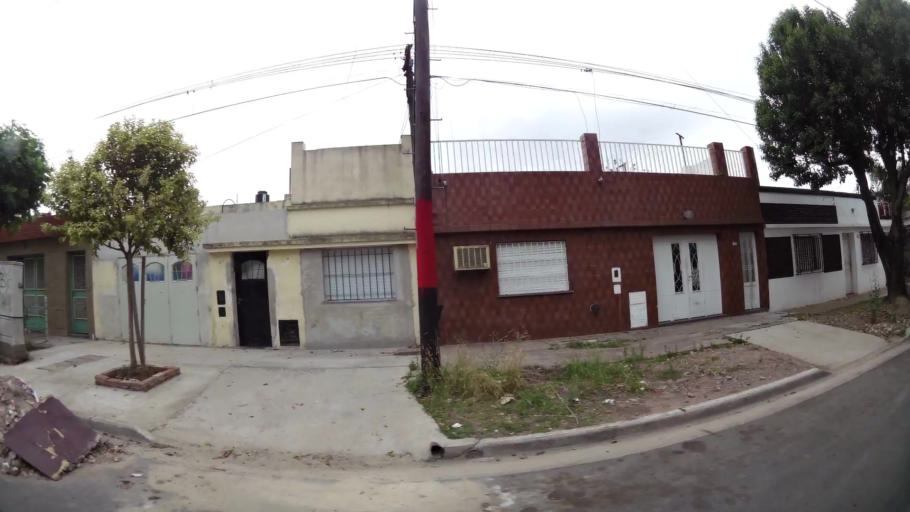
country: AR
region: Santa Fe
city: Gobernador Galvez
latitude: -32.9894
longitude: -60.6606
